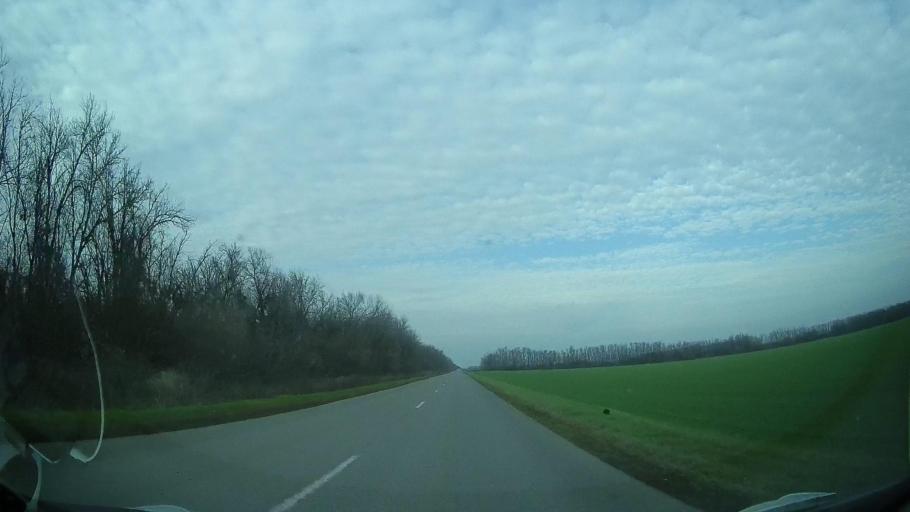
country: RU
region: Rostov
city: Zernograd
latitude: 46.9842
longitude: 40.3916
